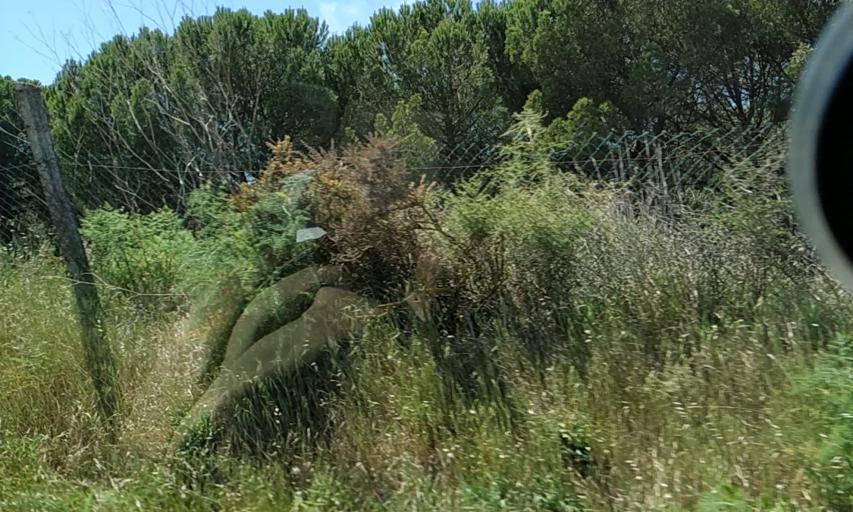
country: PT
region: Santarem
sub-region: Benavente
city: Poceirao
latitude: 38.6892
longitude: -8.7306
